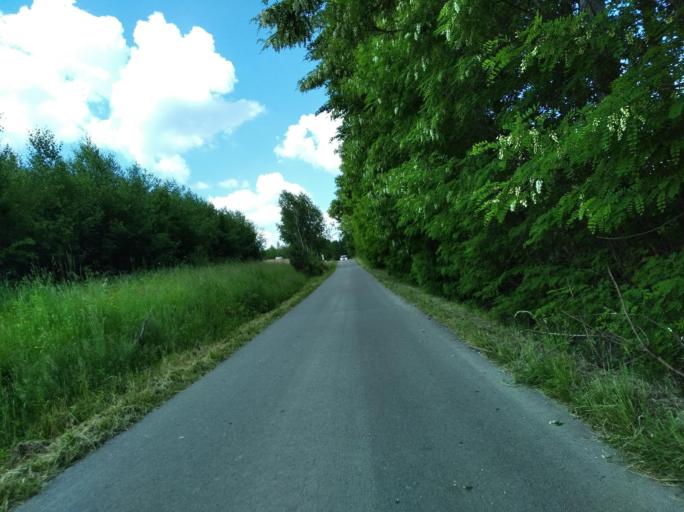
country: PL
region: Subcarpathian Voivodeship
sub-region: Powiat ropczycko-sedziszowski
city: Zagorzyce
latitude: 49.9658
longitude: 21.7152
